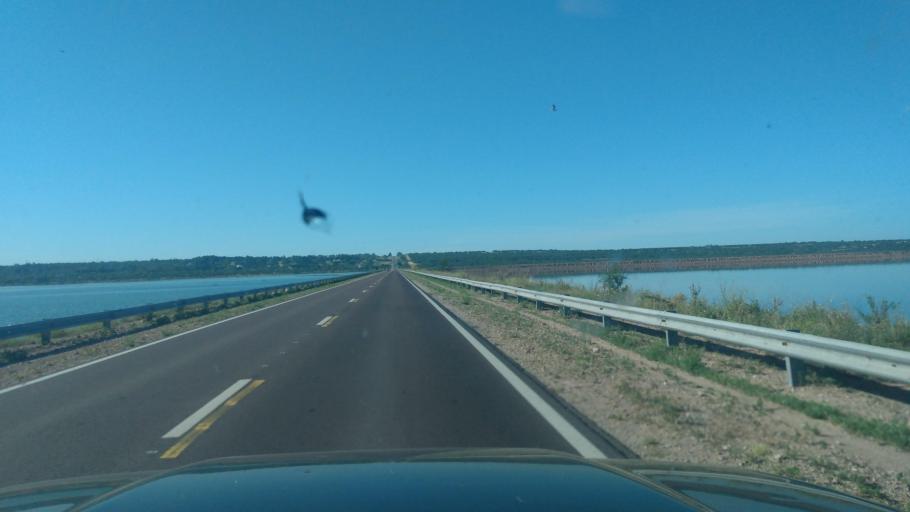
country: AR
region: La Pampa
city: Santa Rosa
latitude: -36.7078
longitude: -64.2831
